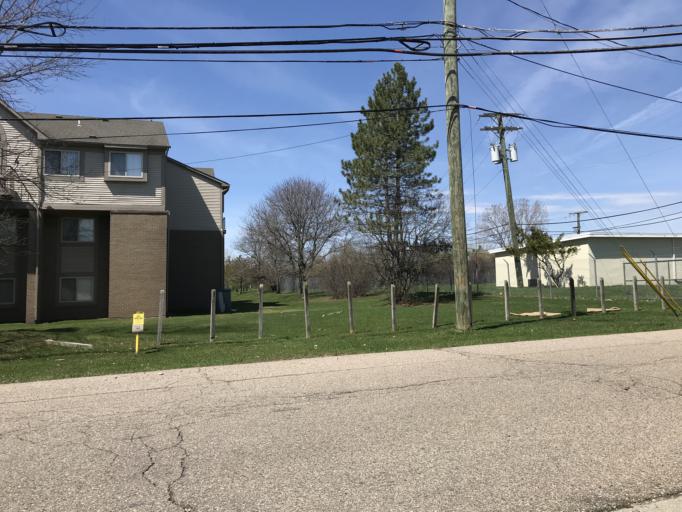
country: US
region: Michigan
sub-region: Oakland County
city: Franklin
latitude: 42.4875
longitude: -83.3052
